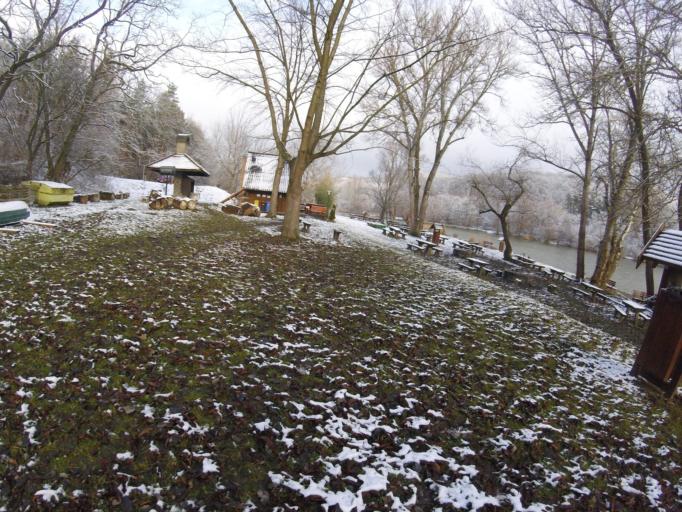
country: HU
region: Komarom-Esztergom
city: Esztergom
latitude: 47.8011
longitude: 18.8053
